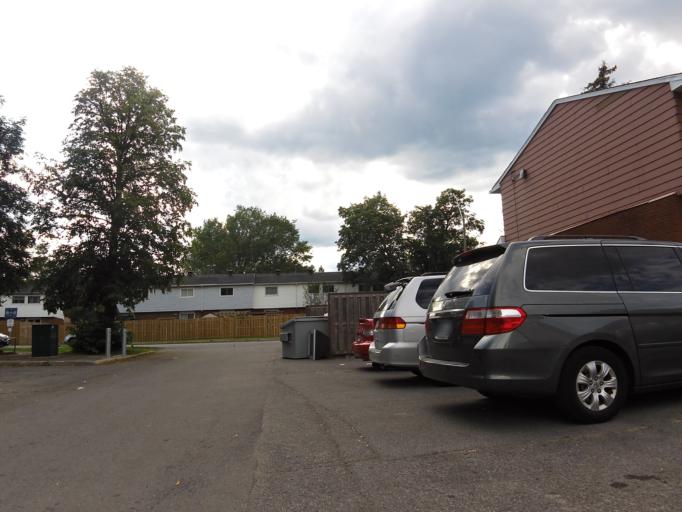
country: CA
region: Ontario
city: Bells Corners
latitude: 45.3449
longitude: -75.7904
